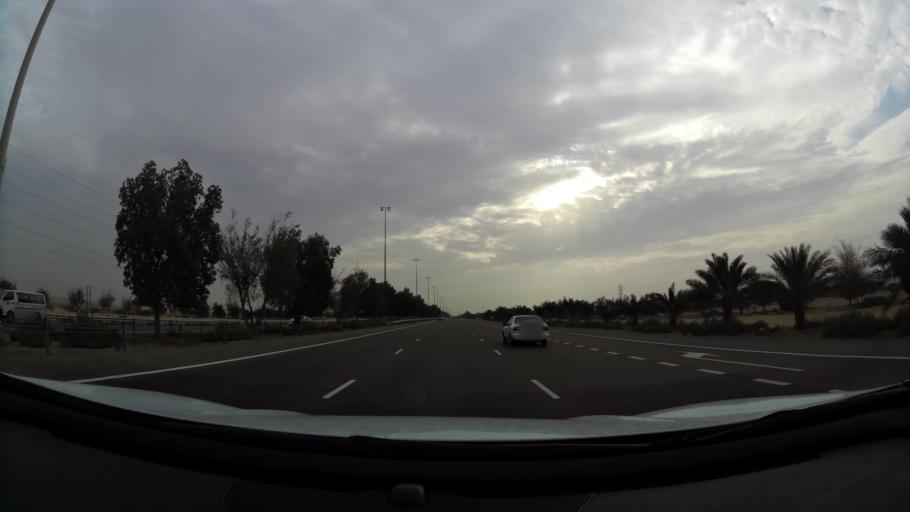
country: AE
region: Abu Dhabi
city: Abu Dhabi
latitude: 24.2204
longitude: 54.8351
